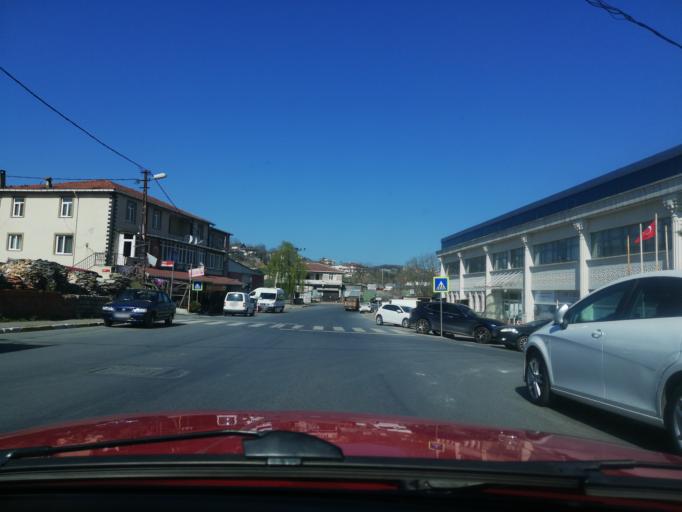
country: TR
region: Istanbul
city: Mahmut Sevket Pasa
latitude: 41.0941
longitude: 29.1437
